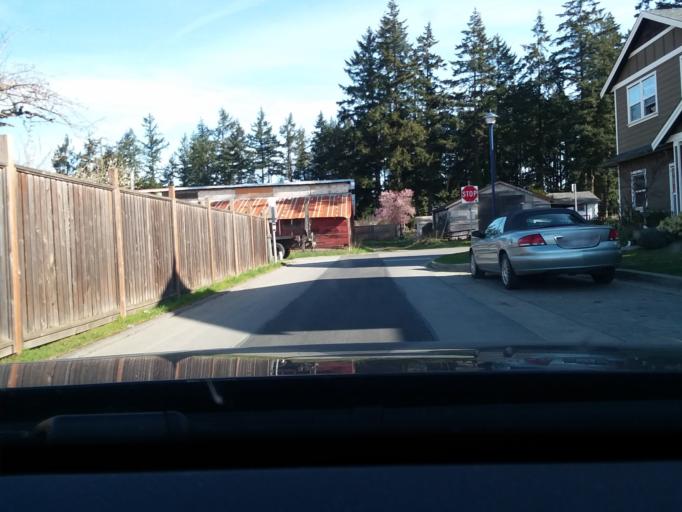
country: CA
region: British Columbia
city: Langford
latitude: 48.4284
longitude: -123.5336
